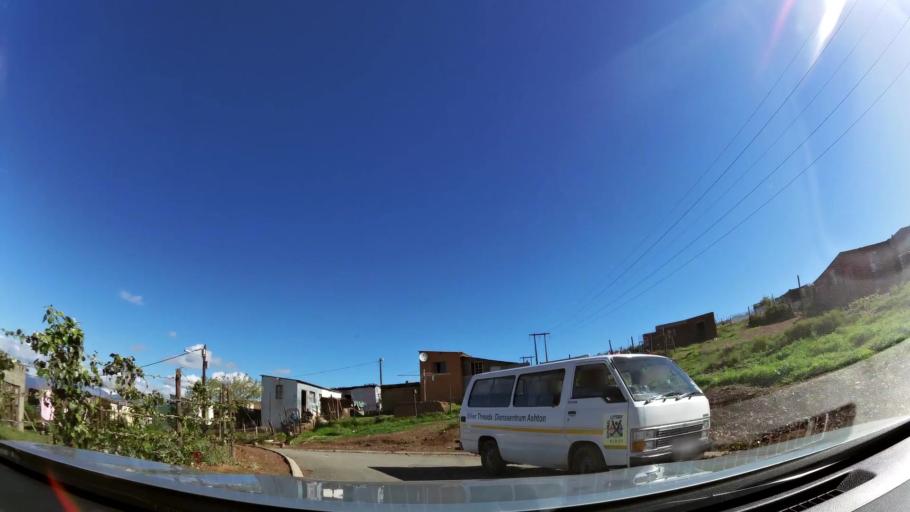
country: ZA
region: Western Cape
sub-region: Cape Winelands District Municipality
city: Ashton
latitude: -33.8299
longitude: 20.0420
